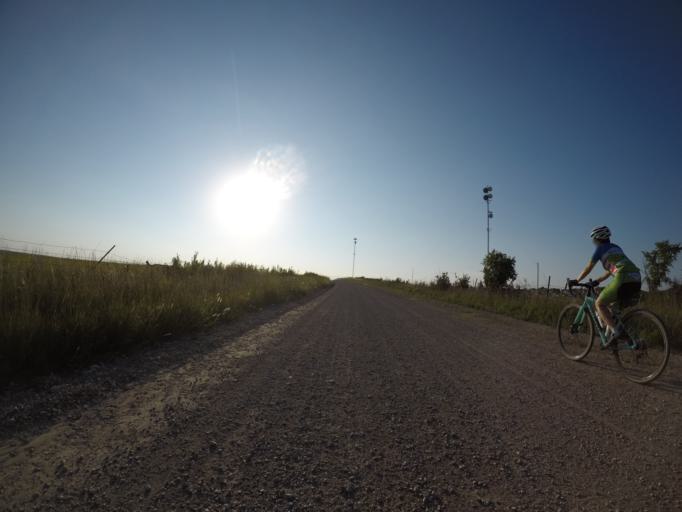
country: US
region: Kansas
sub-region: Riley County
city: Ogden
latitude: 39.0486
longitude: -96.6813
